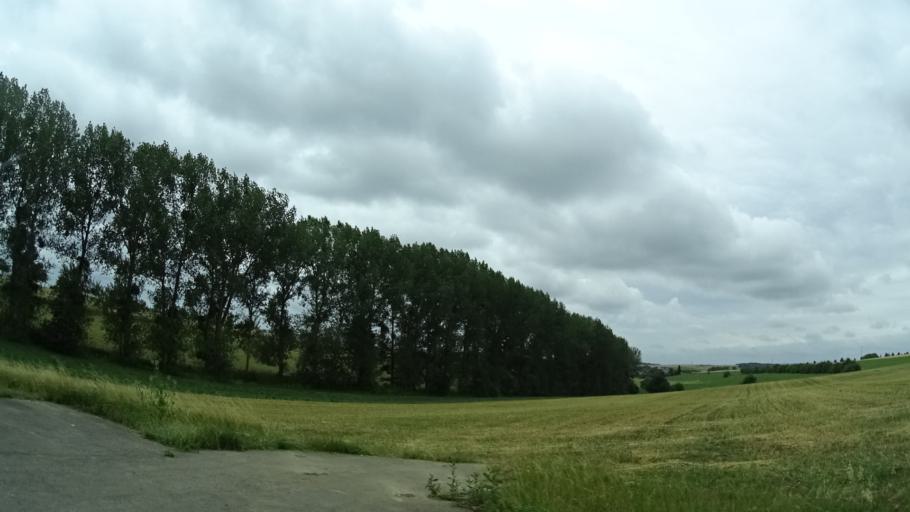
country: LU
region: Grevenmacher
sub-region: Canton de Remich
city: Mondorf-les-Bains
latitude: 49.4941
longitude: 6.2979
